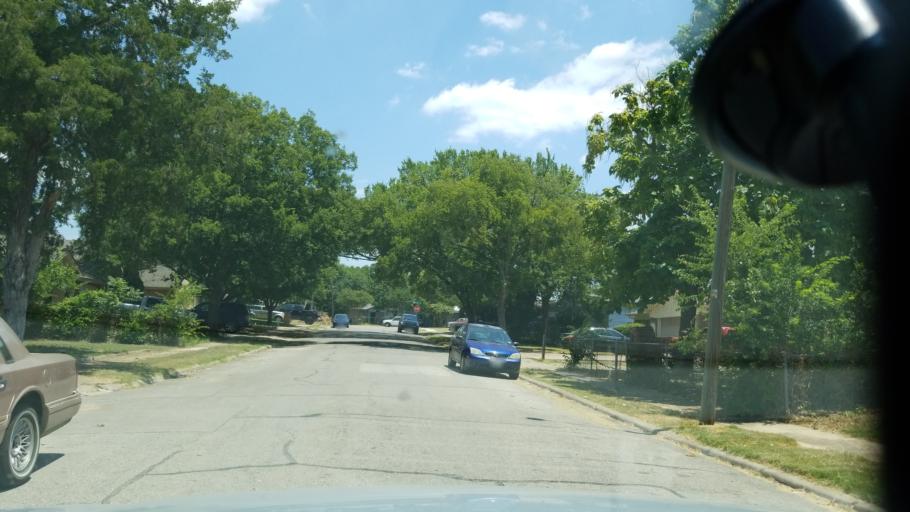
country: US
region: Texas
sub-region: Dallas County
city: Grand Prairie
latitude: 32.7541
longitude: -96.9672
